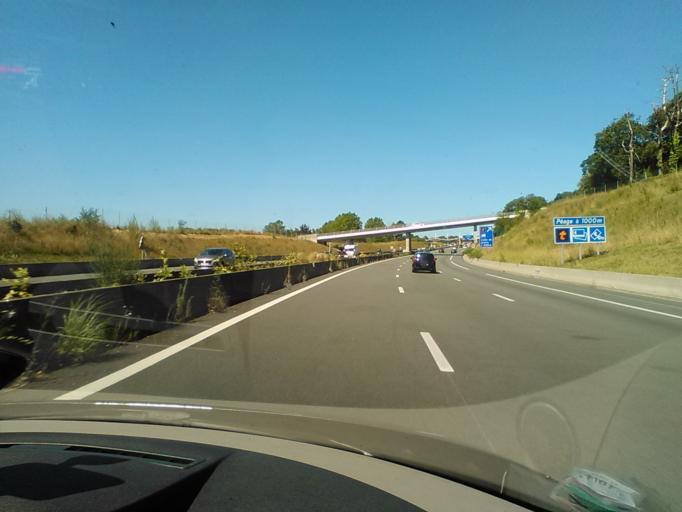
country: FR
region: Aquitaine
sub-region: Departement des Pyrenees-Atlantiques
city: Arbonne
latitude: 43.4471
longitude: -1.5422
